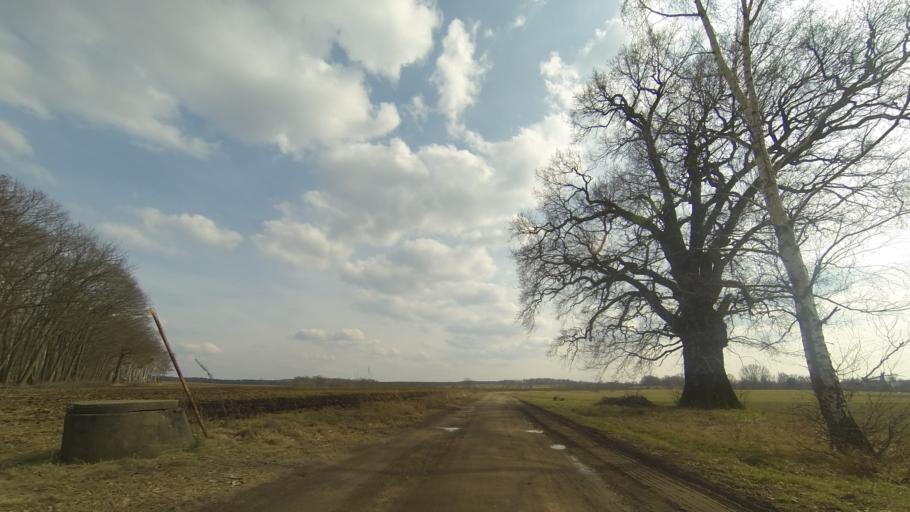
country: DE
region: Saxony
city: Radeburg
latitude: 51.2467
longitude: 13.7045
